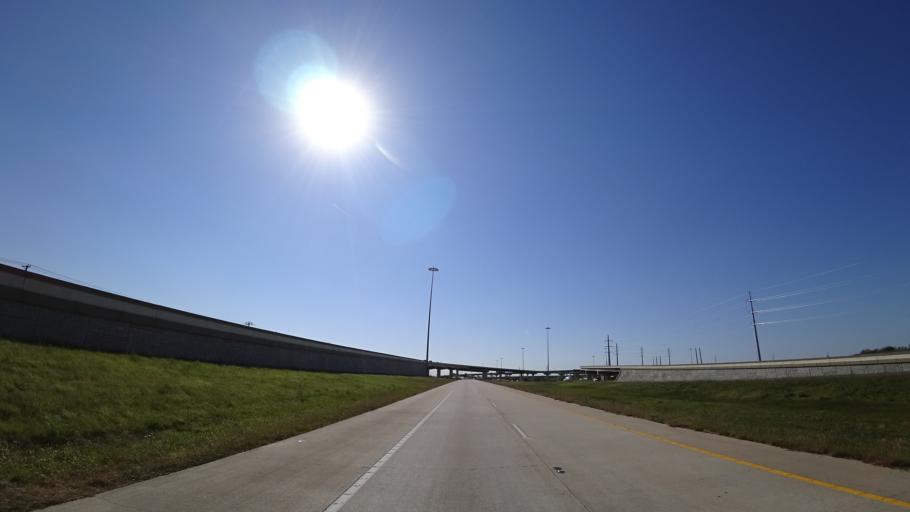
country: US
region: Texas
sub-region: Travis County
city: Pflugerville
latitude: 30.4780
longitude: -97.5886
